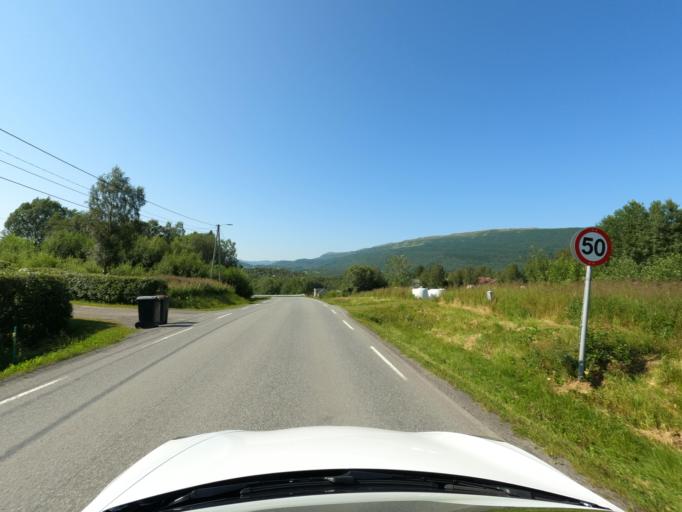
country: NO
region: Nordland
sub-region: Ballangen
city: Ballangen
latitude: 68.3456
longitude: 16.8385
